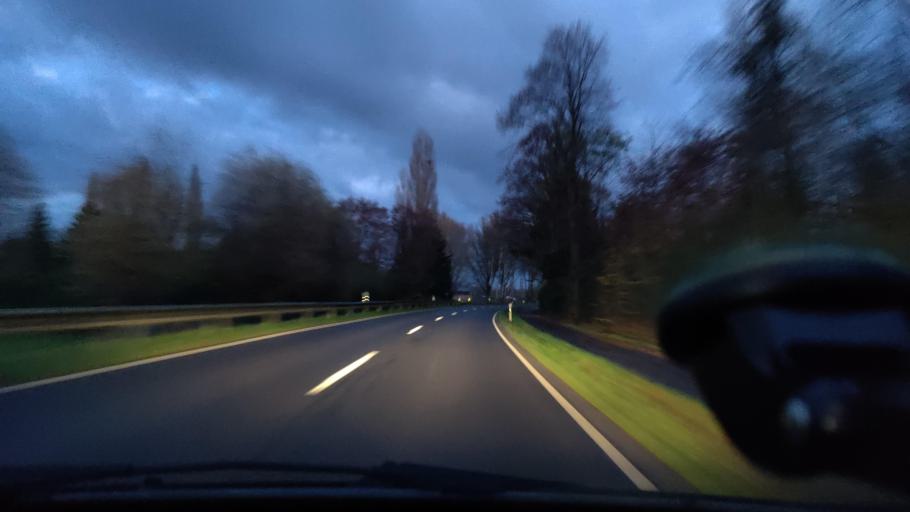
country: DE
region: North Rhine-Westphalia
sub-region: Regierungsbezirk Dusseldorf
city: Uedem
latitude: 51.6111
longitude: 6.3092
